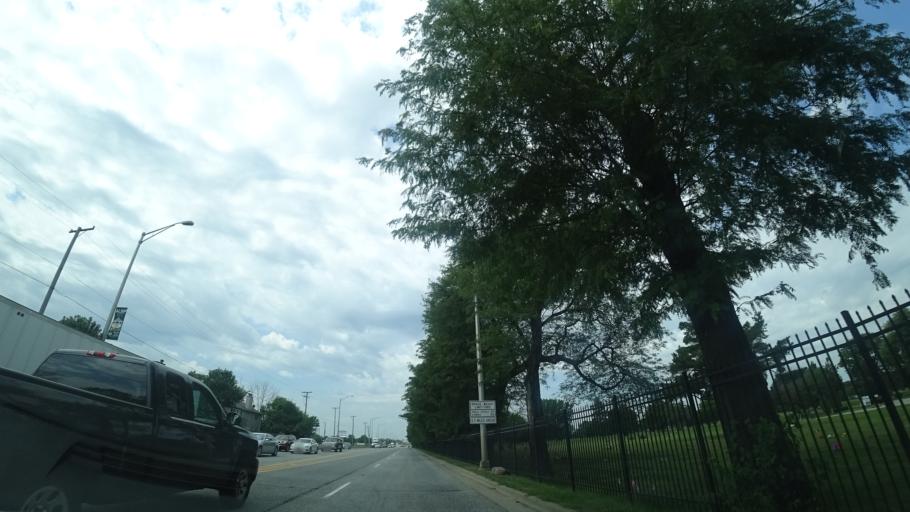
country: US
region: Illinois
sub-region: Cook County
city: Alsip
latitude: 41.6619
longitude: -87.7291
